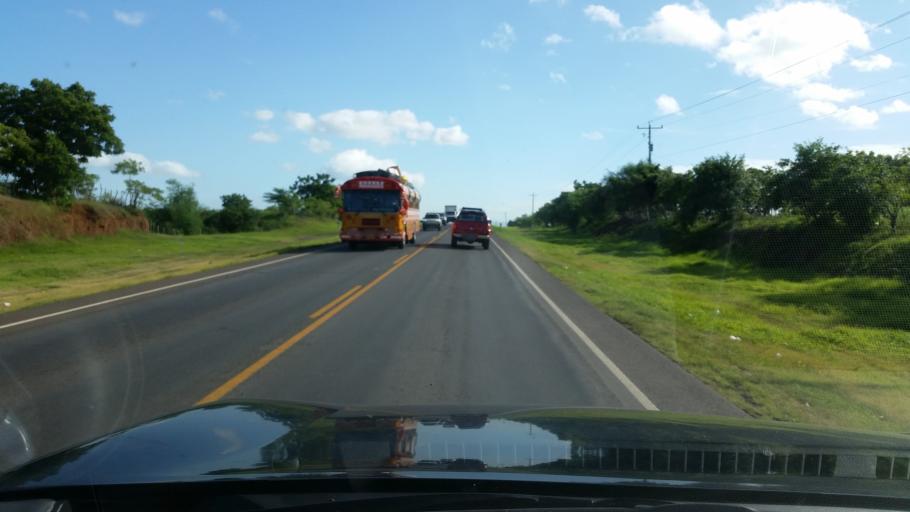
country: NI
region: Managua
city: Tipitapa
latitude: 12.3198
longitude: -86.0534
